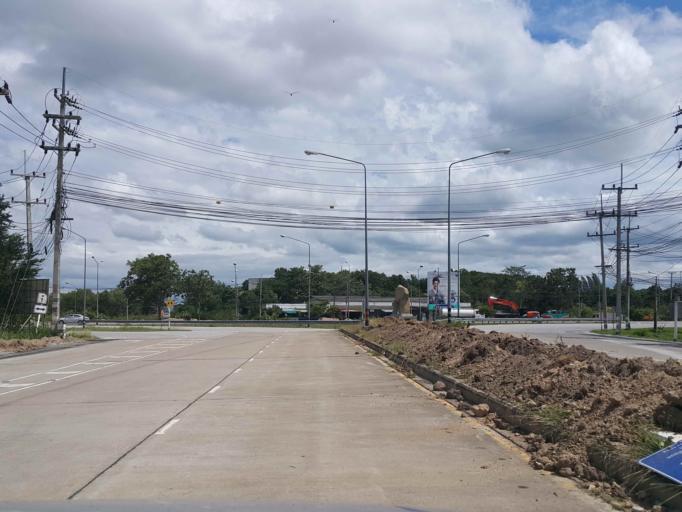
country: TH
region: Tak
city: Tak
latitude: 16.8542
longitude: 99.1174
